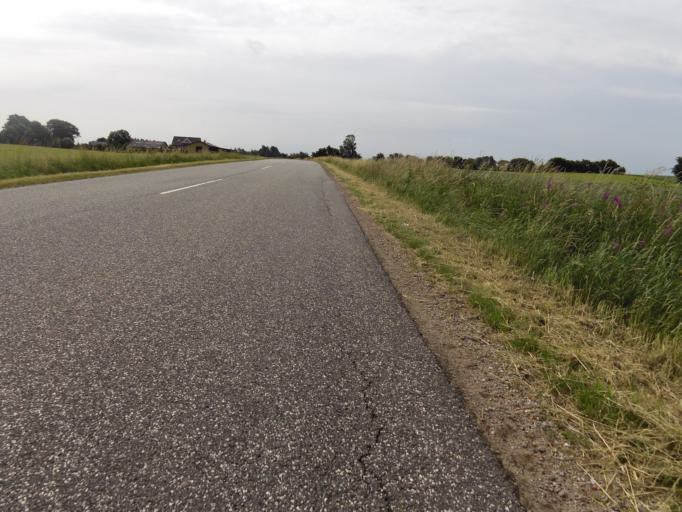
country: DK
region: Central Jutland
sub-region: Holstebro Kommune
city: Holstebro
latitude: 56.4325
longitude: 8.6298
